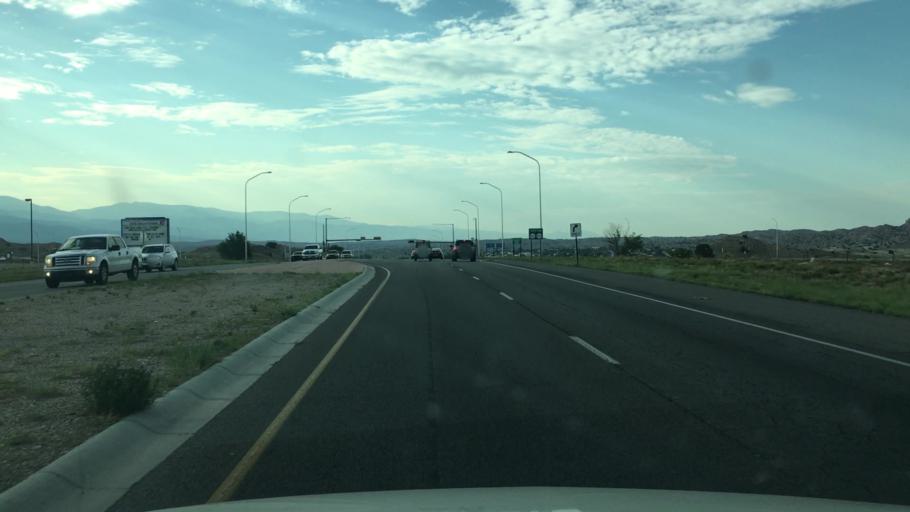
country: US
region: New Mexico
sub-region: Santa Fe County
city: El Valle de Arroyo Seco
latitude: 35.9784
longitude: -106.0461
